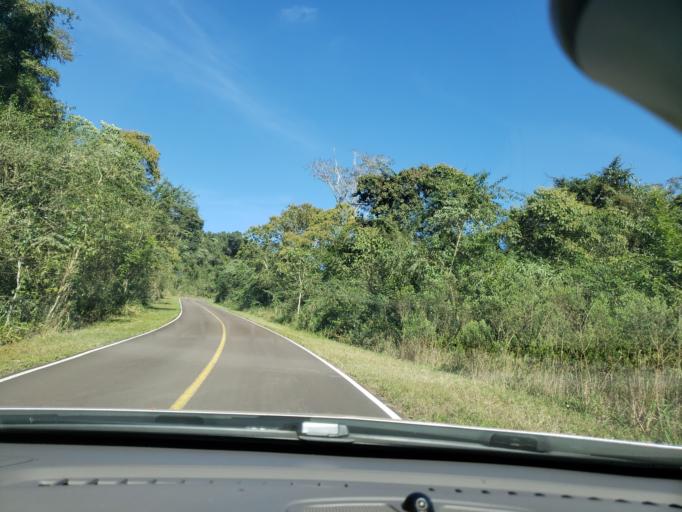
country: BR
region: Rio Grande do Sul
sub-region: Tres Passos
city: Tres Passos
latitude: -27.1476
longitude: -53.9098
